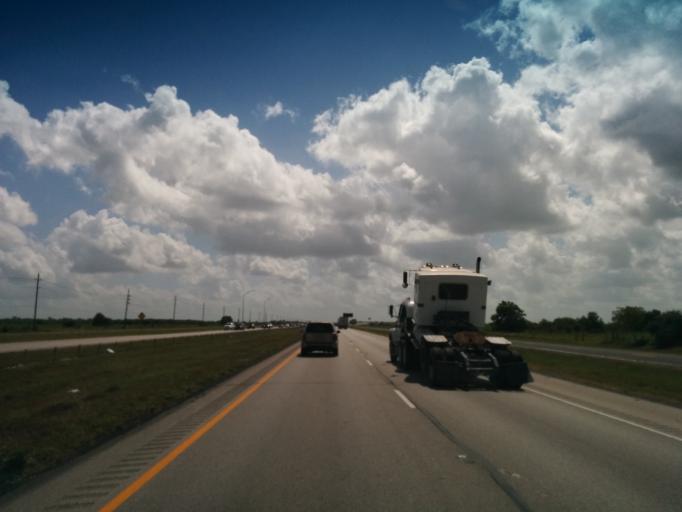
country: US
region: Texas
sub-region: Austin County
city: Sealy
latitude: 29.7618
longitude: -96.2016
